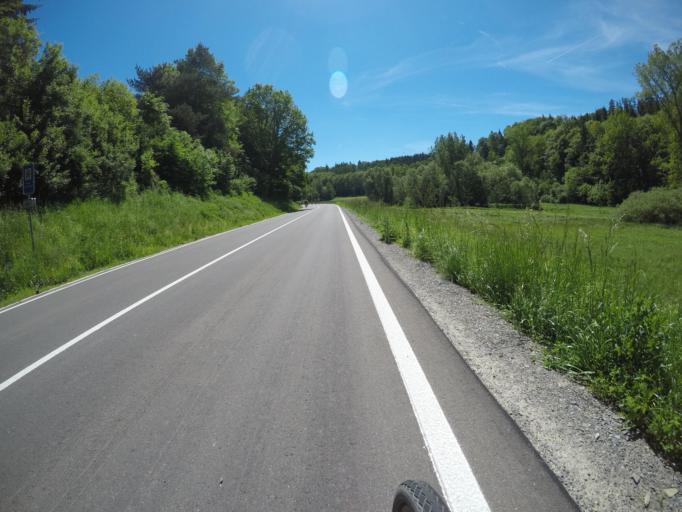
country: DE
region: Baden-Wuerttemberg
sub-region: Karlsruhe Region
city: Neuhausen
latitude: 48.8059
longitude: 8.8125
